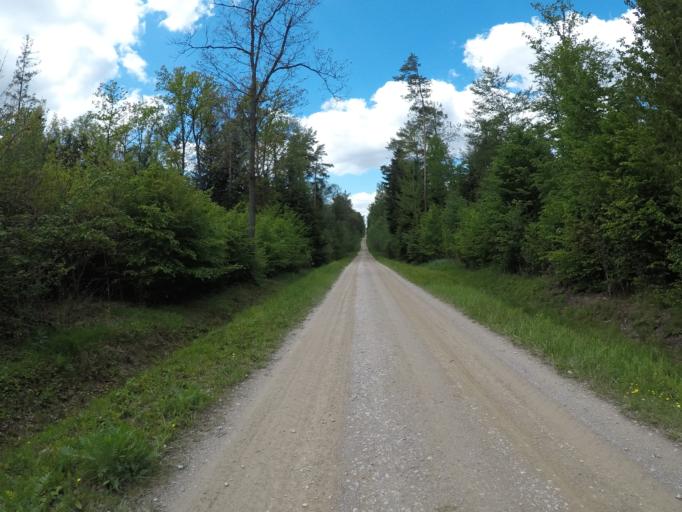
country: PL
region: Swietokrzyskie
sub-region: Powiat kielecki
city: Kostomloty Pierwsze
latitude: 50.9317
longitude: 20.6314
